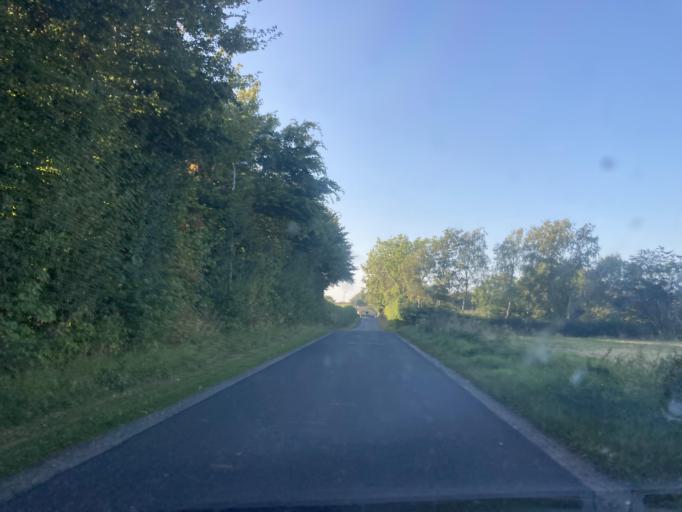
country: DK
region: South Denmark
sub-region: Svendborg Kommune
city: Thuro By
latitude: 55.1176
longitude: 10.7315
